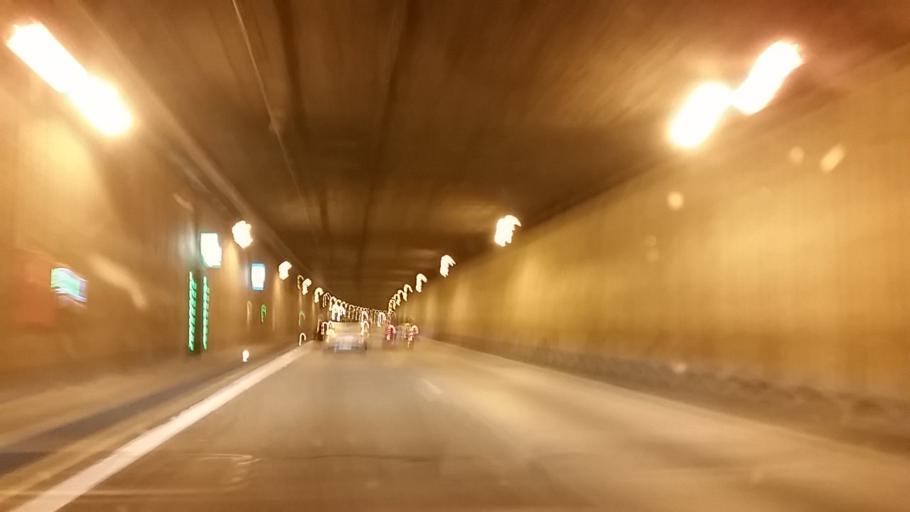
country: DE
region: North Rhine-Westphalia
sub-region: Regierungsbezirk Dusseldorf
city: Dusseldorf
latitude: 51.2278
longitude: 6.7455
